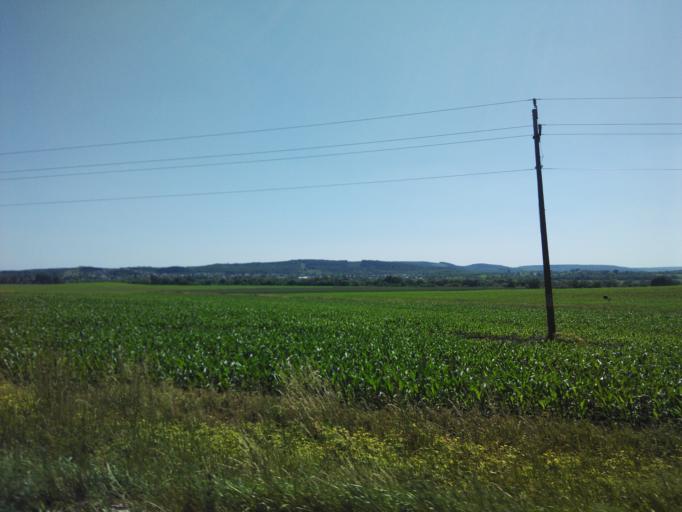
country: HU
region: Fejer
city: Bodajk
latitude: 47.3431
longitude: 18.2370
